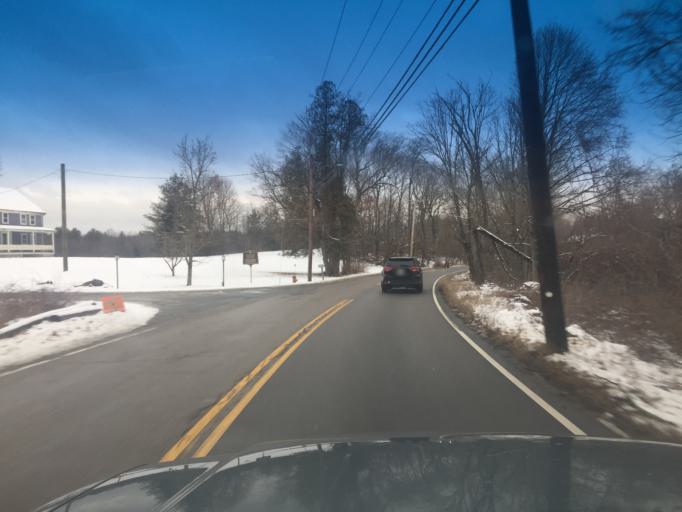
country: US
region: Massachusetts
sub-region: Norfolk County
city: Millis
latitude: 42.1813
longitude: -71.3630
